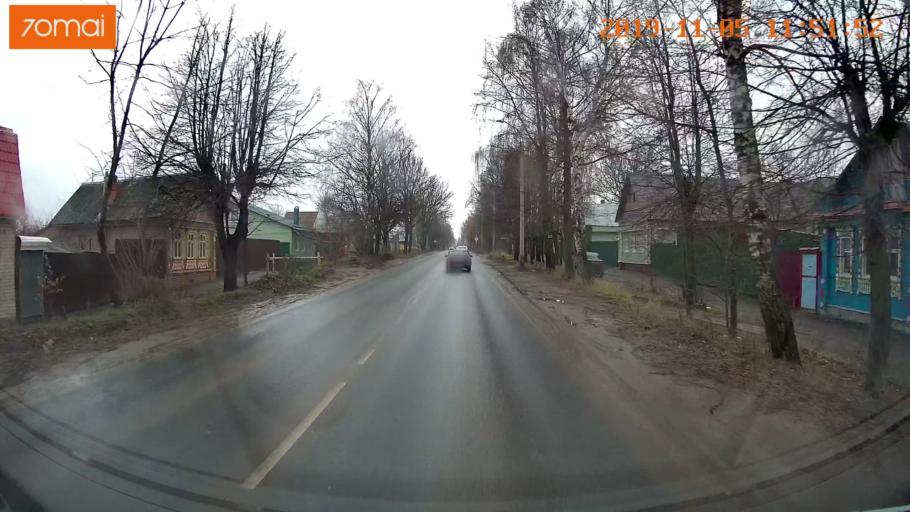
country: RU
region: Ivanovo
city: Bogorodskoye
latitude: 57.0032
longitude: 41.0288
